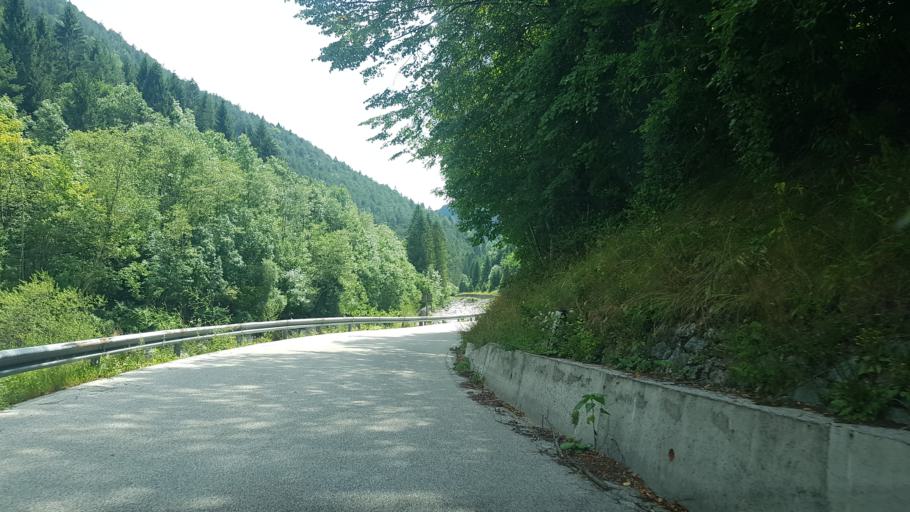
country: IT
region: Friuli Venezia Giulia
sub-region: Provincia di Udine
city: Moggio Udinese
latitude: 46.4871
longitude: 13.1943
